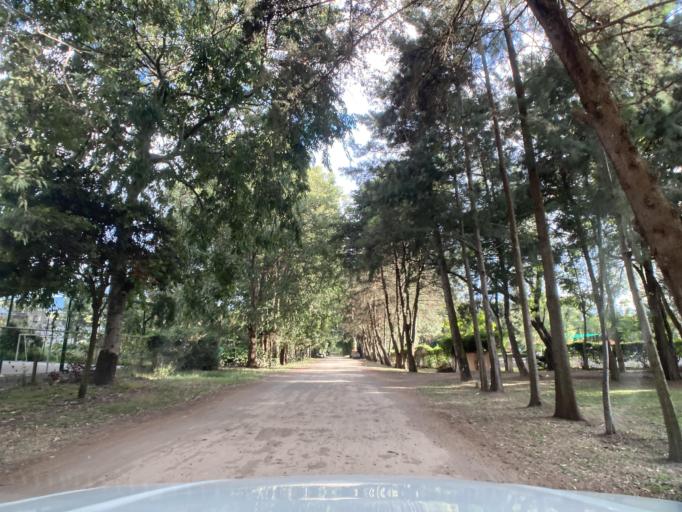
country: GT
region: Sacatepequez
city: Jocotenango
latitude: 14.5733
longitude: -90.7453
